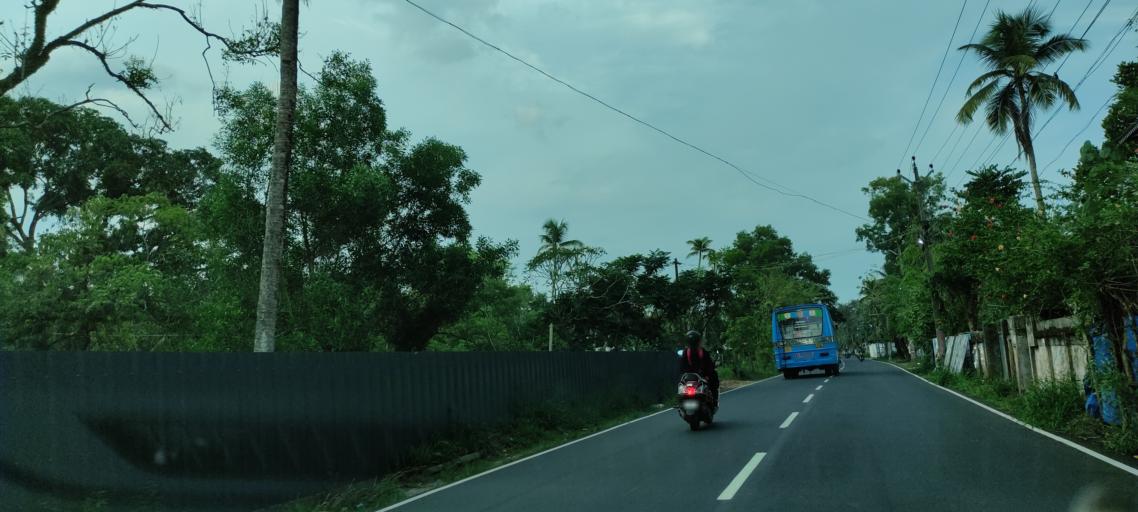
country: IN
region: Kerala
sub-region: Alappuzha
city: Kutiatodu
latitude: 9.7881
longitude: 76.3592
